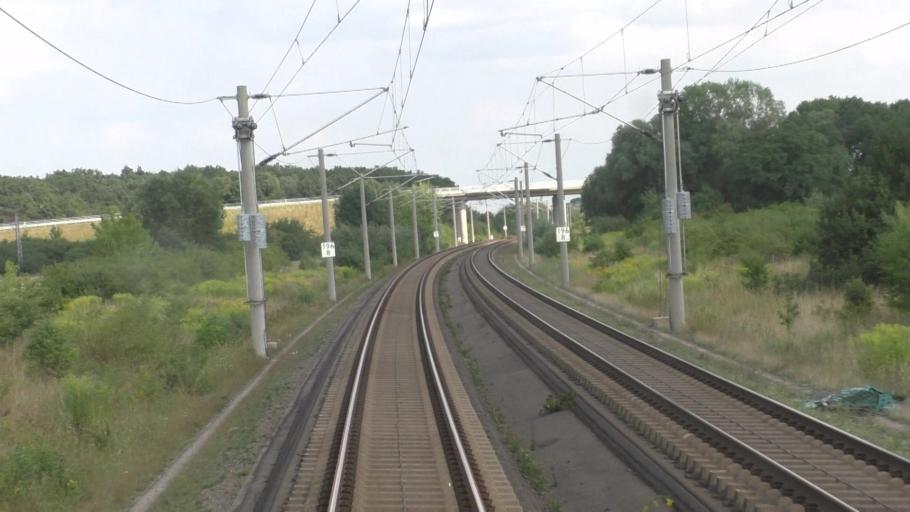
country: DE
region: Saxony-Anhalt
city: Tangermunde
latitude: 52.6009
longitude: 11.9739
